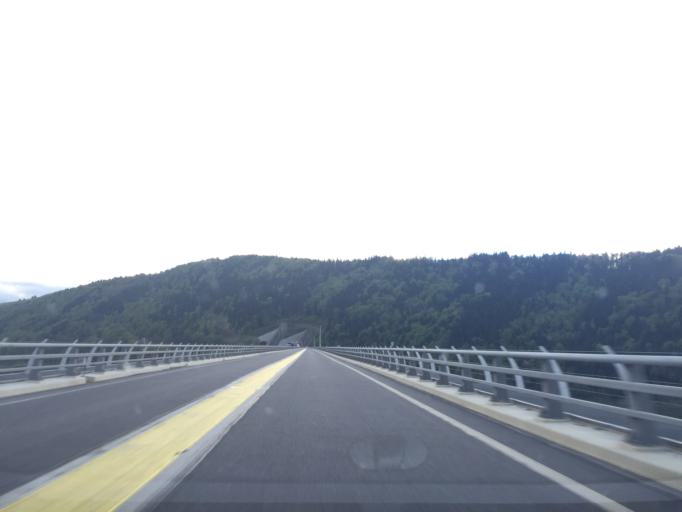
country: FR
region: Rhone-Alpes
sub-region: Departement de l'Isere
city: La Motte-Saint-Martin
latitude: 44.9285
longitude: 5.6344
